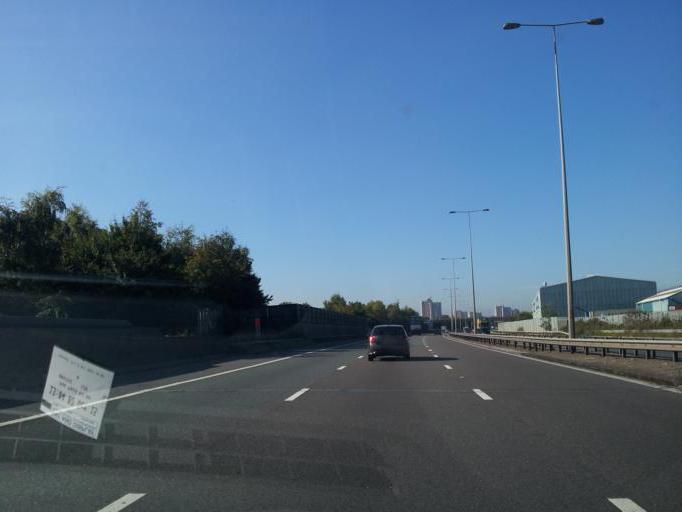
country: GB
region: England
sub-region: Manchester
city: Failsworth
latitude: 53.5275
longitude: -2.1703
